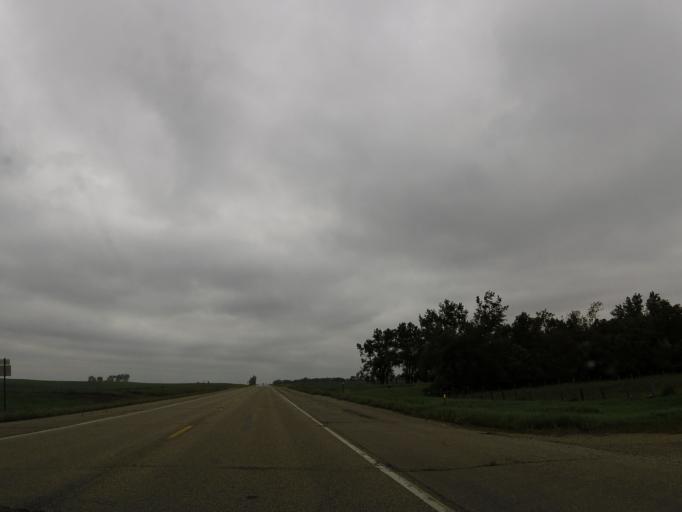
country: US
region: South Dakota
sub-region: Deuel County
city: Clear Lake
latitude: 44.9332
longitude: -96.6166
